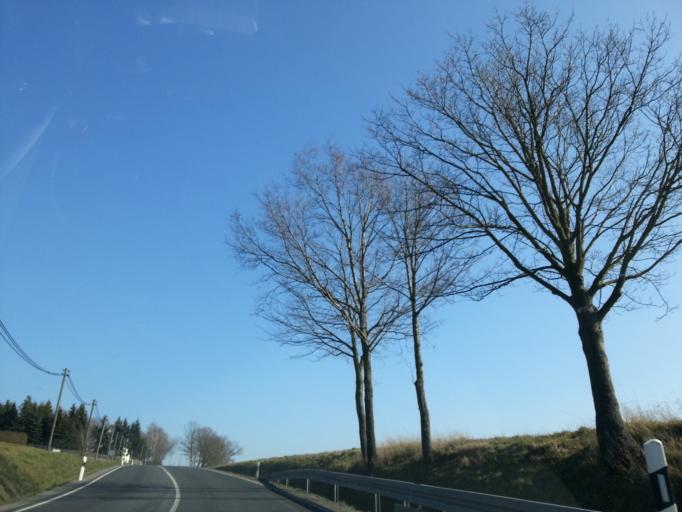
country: DE
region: Saxony
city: Halsbrucke
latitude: 50.9205
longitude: 13.3799
